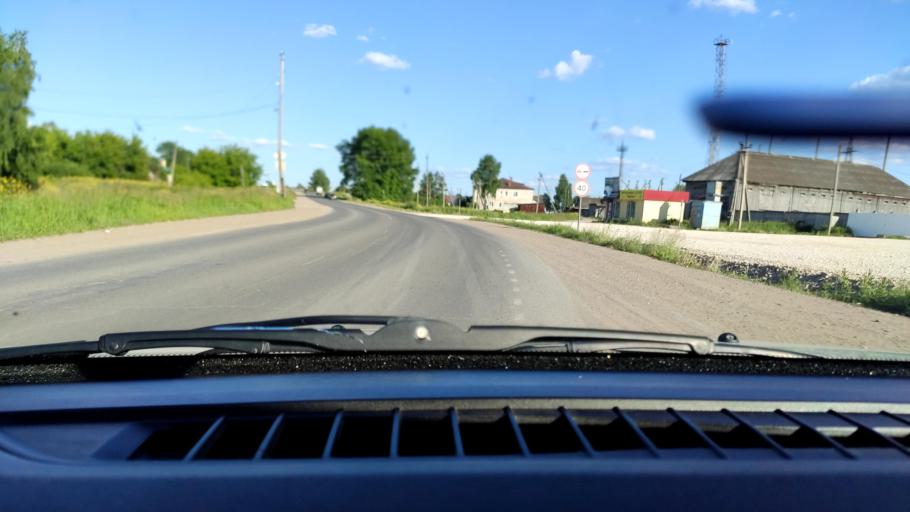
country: RU
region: Perm
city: Orda
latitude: 57.1910
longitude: 56.9054
